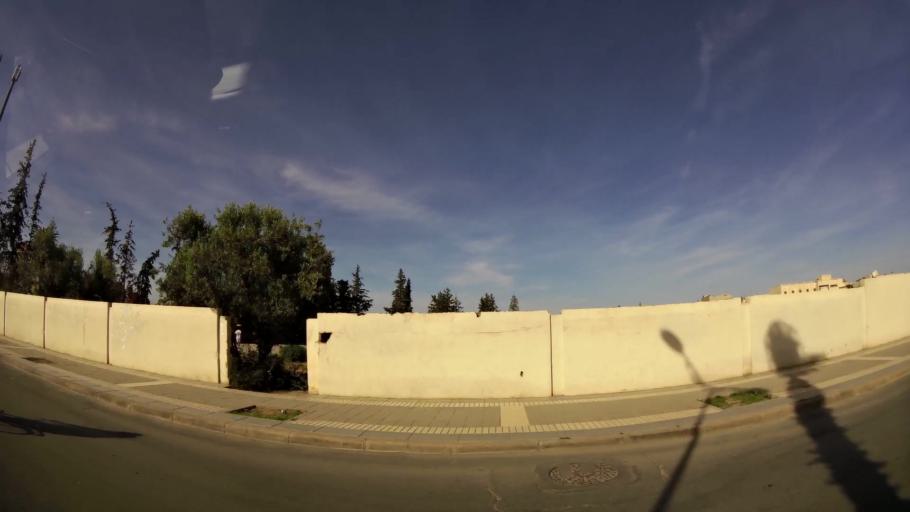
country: MA
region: Oriental
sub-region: Oujda-Angad
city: Oujda
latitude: 34.6657
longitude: -1.8964
